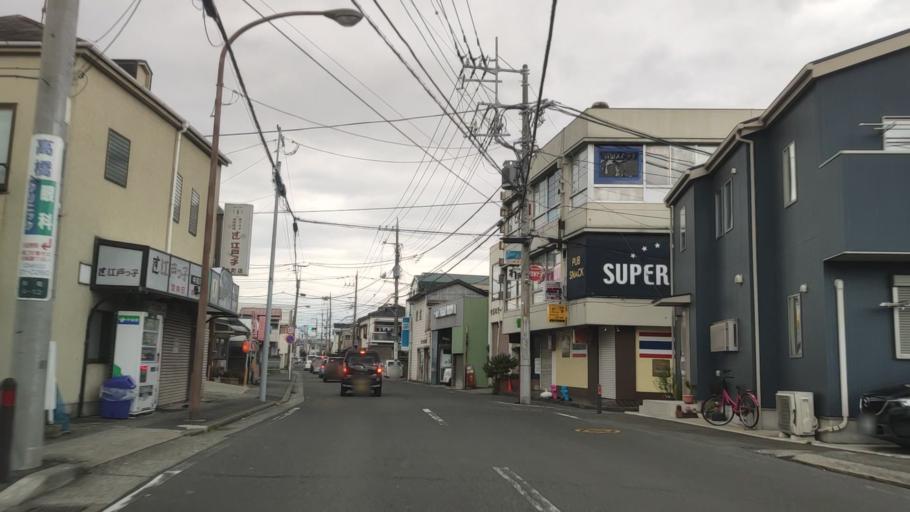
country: JP
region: Kanagawa
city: Odawara
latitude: 35.2576
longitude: 139.1632
